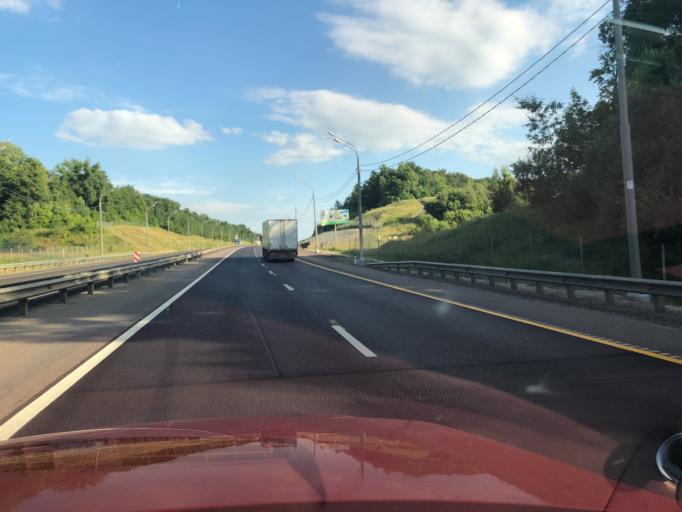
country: RU
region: Lipetsk
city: Zadonsk
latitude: 52.4039
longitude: 38.8566
